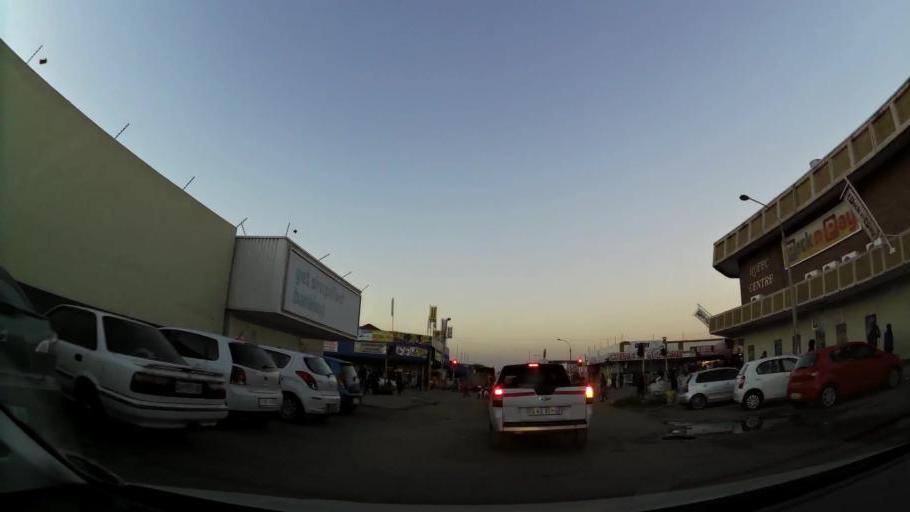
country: ZA
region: North-West
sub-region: Bojanala Platinum District Municipality
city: Rustenburg
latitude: -25.6644
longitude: 27.2380
